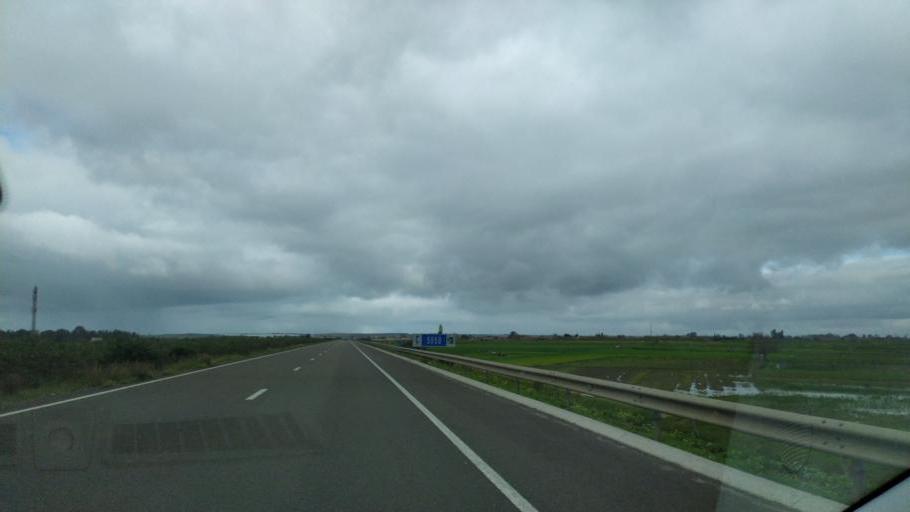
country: MA
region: Gharb-Chrarda-Beni Hssen
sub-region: Kenitra Province
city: Kenitra
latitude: 34.3557
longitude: -6.5140
